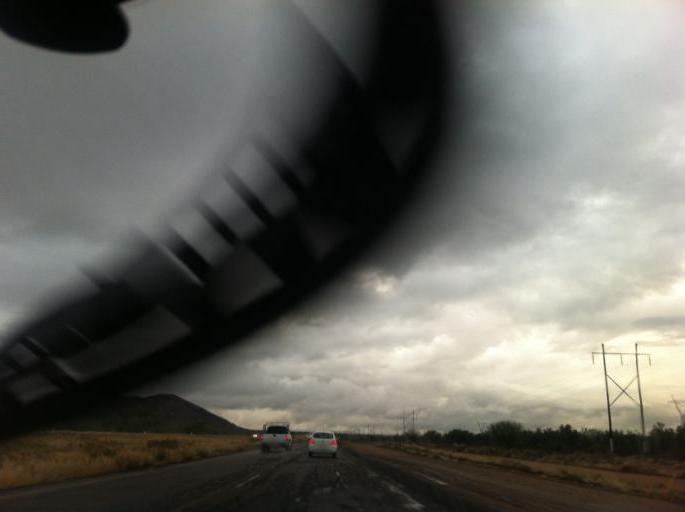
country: MX
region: Sonora
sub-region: San Miguel de Horcasitas
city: Las Mercedes [Agropecuaria]
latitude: 29.5694
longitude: -111.0169
